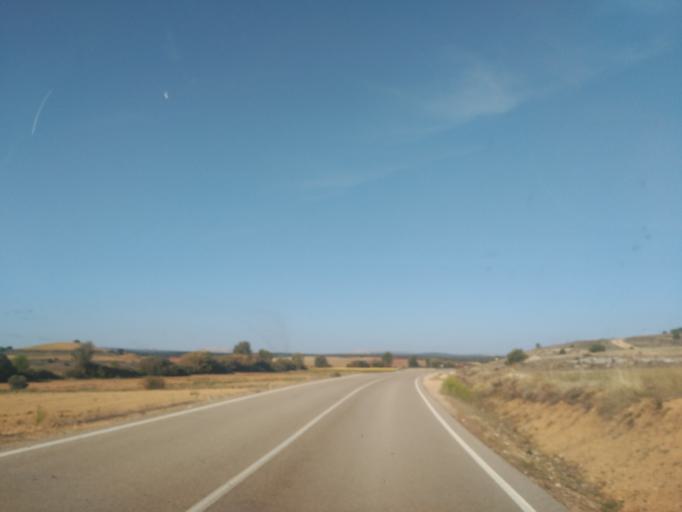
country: ES
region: Castille and Leon
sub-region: Provincia de Soria
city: Alcubilla de Avellaneda
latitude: 41.7514
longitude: -3.2803
